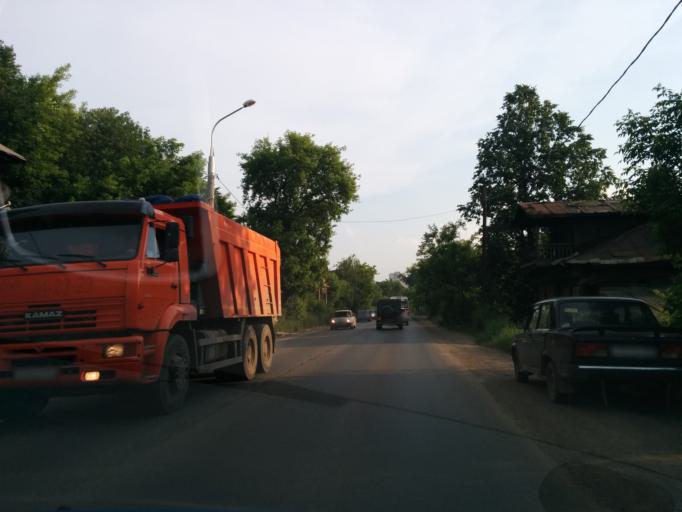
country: RU
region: Perm
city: Perm
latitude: 58.0426
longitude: 56.3190
